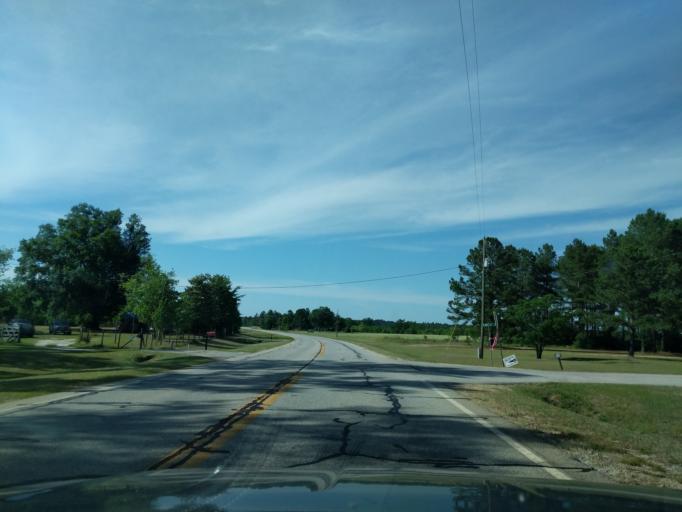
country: US
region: Georgia
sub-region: Jefferson County
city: Wrens
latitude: 33.2622
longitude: -82.3845
